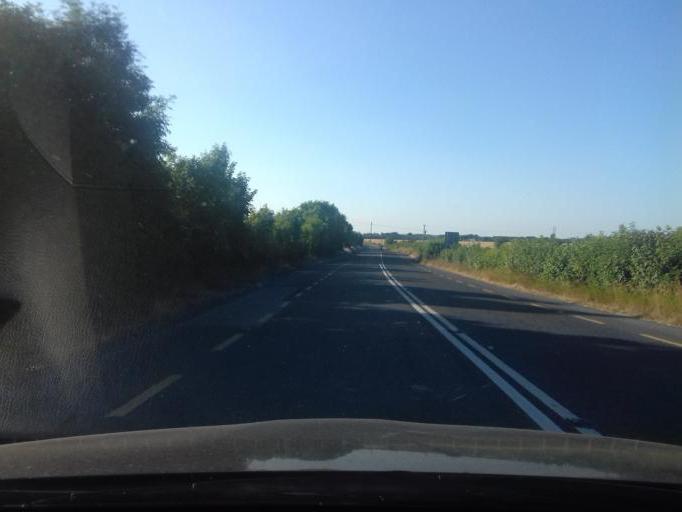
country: IE
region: Leinster
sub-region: Fingal County
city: Blanchardstown
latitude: 53.4465
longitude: -6.3425
